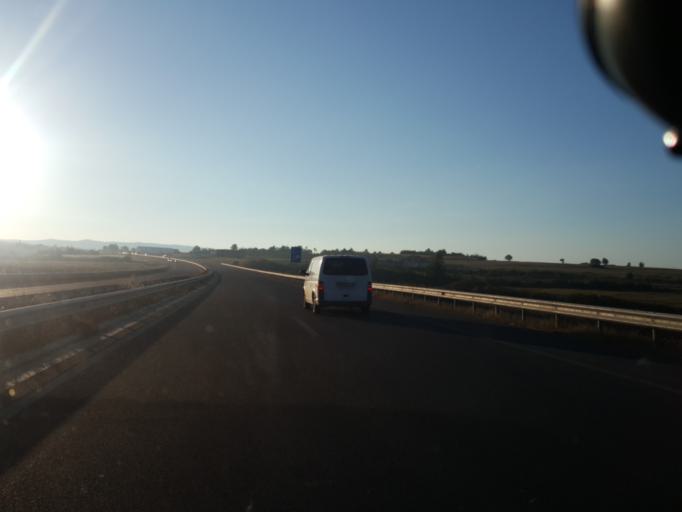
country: XK
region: Prizren
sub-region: Komuna e Malisheves
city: Llazice
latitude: 42.5708
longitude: 20.7336
